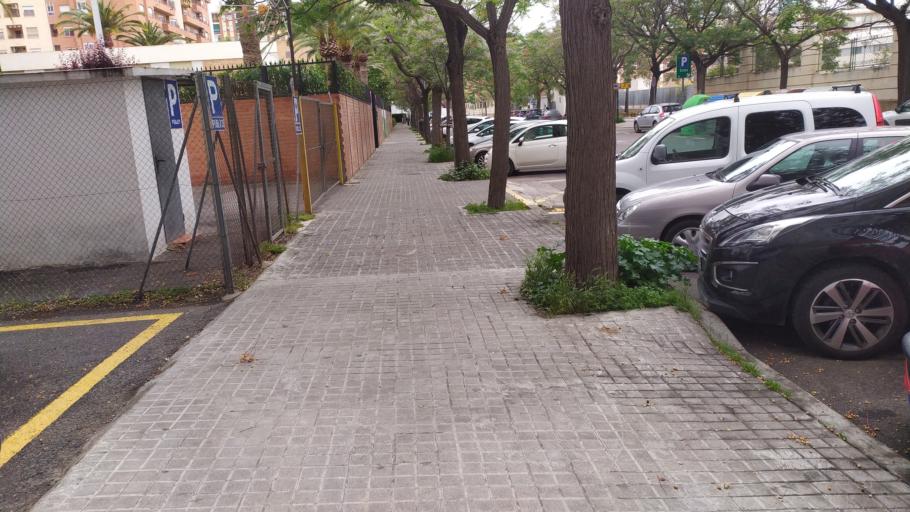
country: ES
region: Valencia
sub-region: Provincia de Valencia
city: Mislata
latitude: 39.4672
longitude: -0.4102
